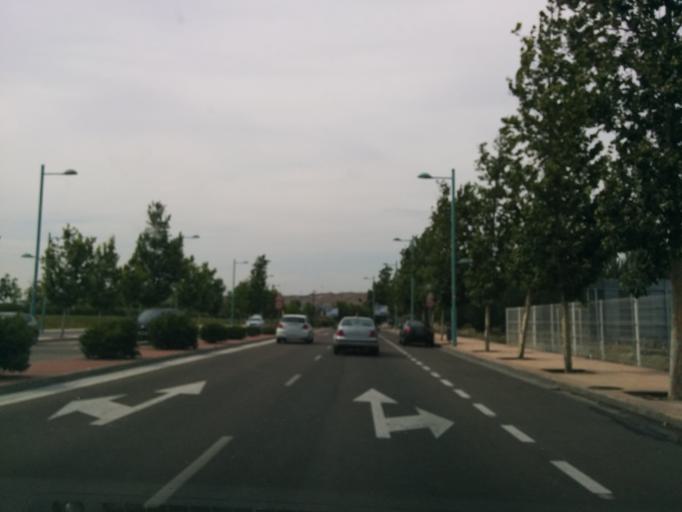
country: ES
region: Aragon
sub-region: Provincia de Zaragoza
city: Almozara
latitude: 41.6771
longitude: -0.8986
